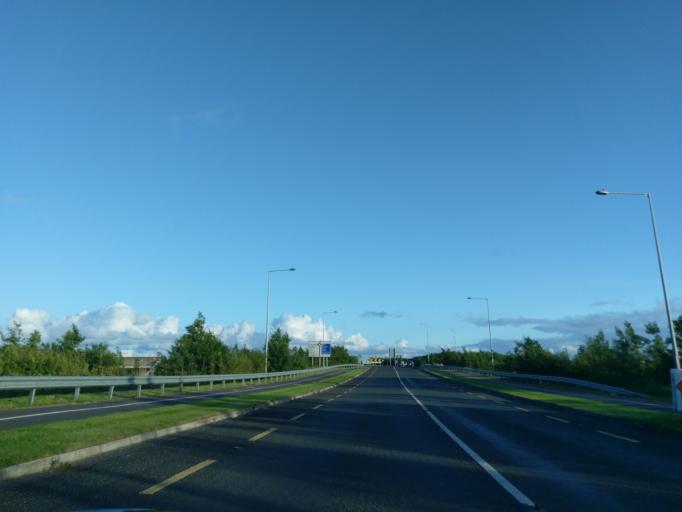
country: IE
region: Connaught
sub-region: County Galway
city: Athenry
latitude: 53.2916
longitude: -8.7568
